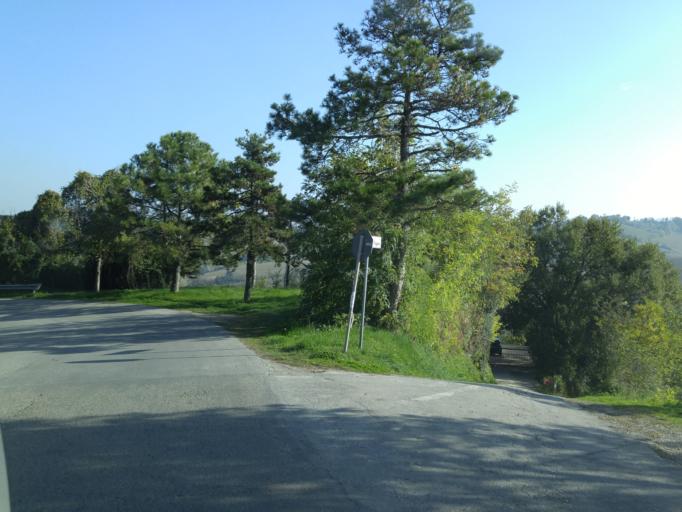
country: IT
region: The Marches
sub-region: Provincia di Pesaro e Urbino
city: Montemaggiore al Metauro
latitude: 43.7368
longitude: 12.9490
